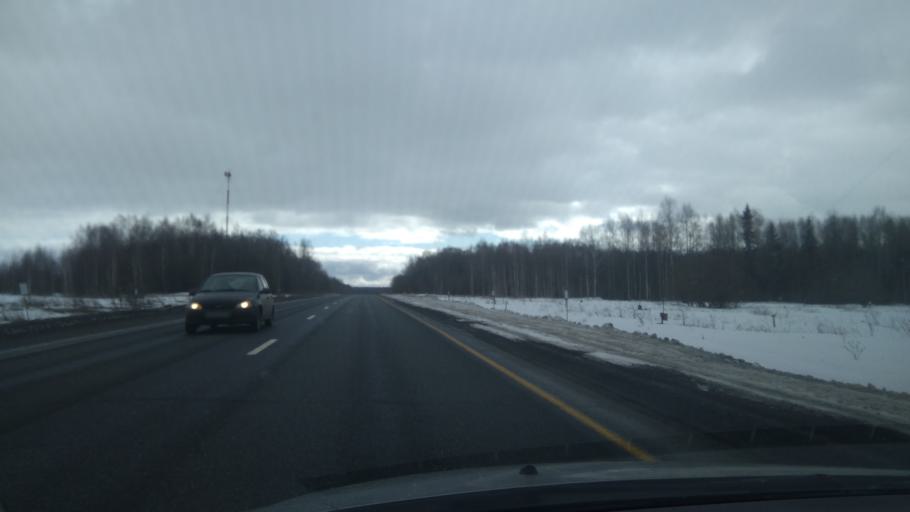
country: RU
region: Perm
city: Orda
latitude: 57.1959
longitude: 57.1130
